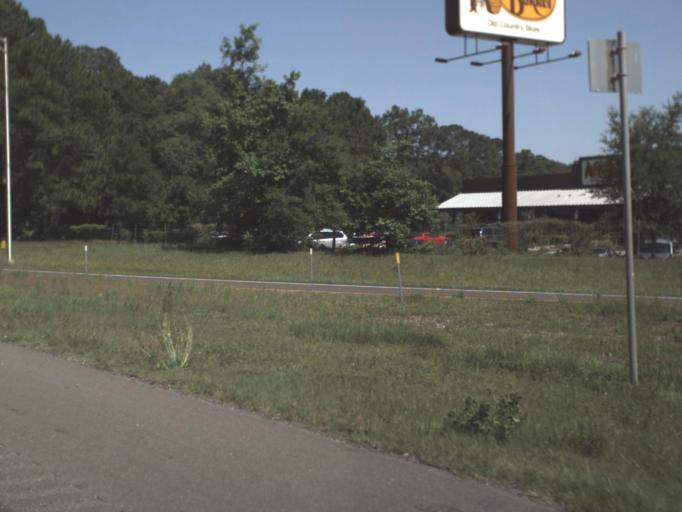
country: US
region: Florida
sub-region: Duval County
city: Baldwin
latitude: 30.3092
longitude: -81.8453
